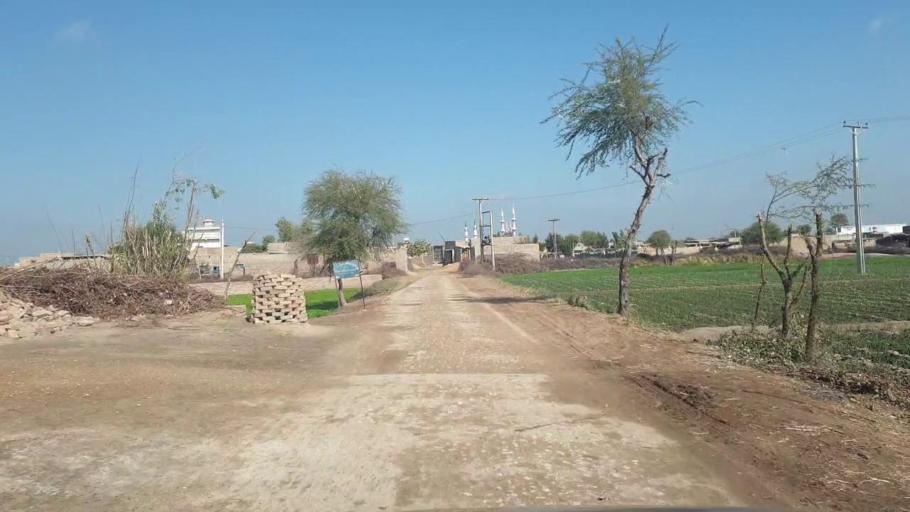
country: PK
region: Sindh
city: Bhit Shah
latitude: 25.8938
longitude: 68.5270
